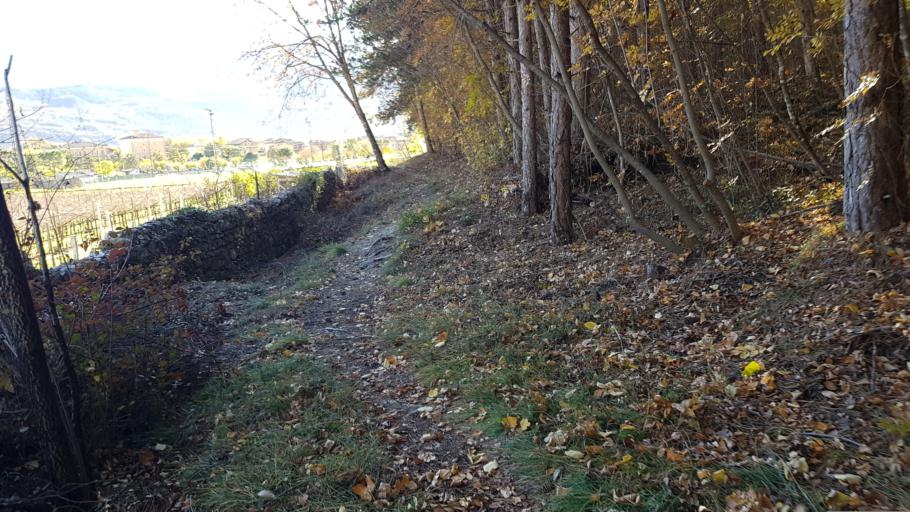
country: IT
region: Trentino-Alto Adige
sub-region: Provincia di Trento
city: Pietramurata
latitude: 46.0265
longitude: 10.9404
